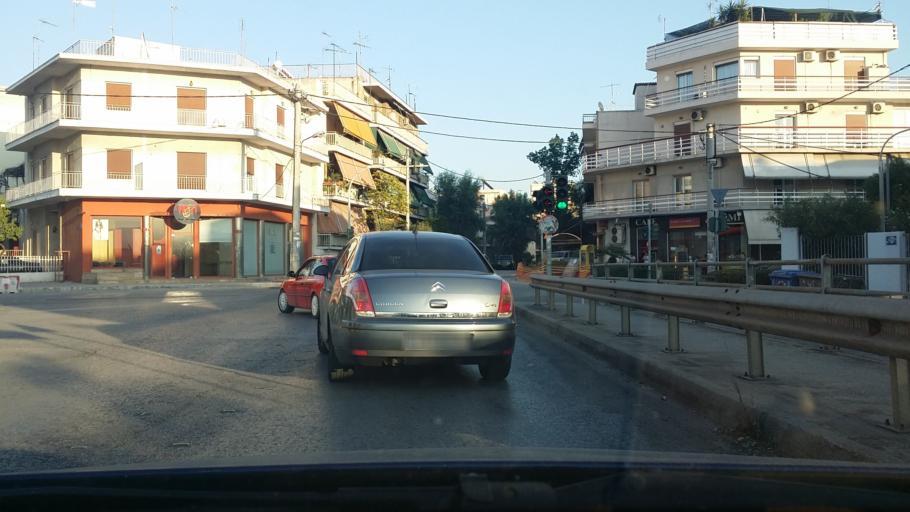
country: GR
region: Attica
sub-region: Nomarchia Athinas
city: Nea Chalkidona
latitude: 38.0261
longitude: 23.7278
